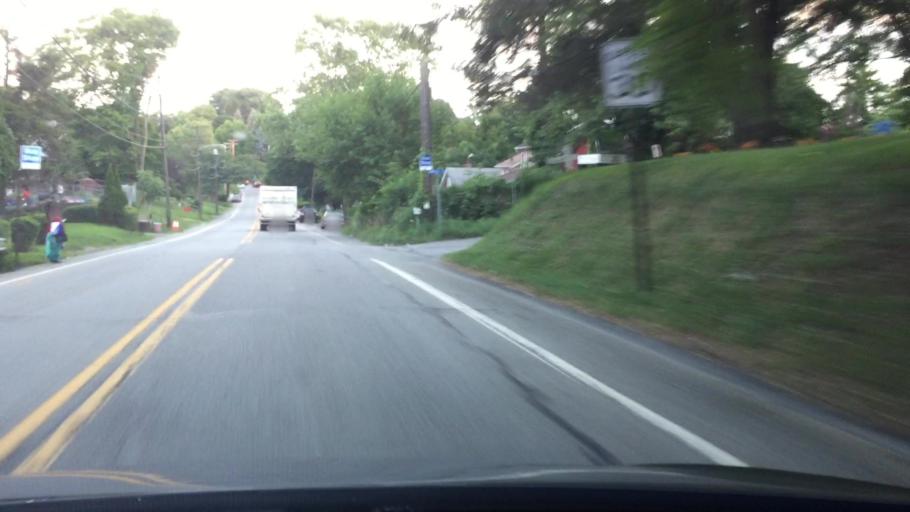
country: US
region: Pennsylvania
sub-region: Allegheny County
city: Churchill
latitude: 40.4629
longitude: -79.8503
